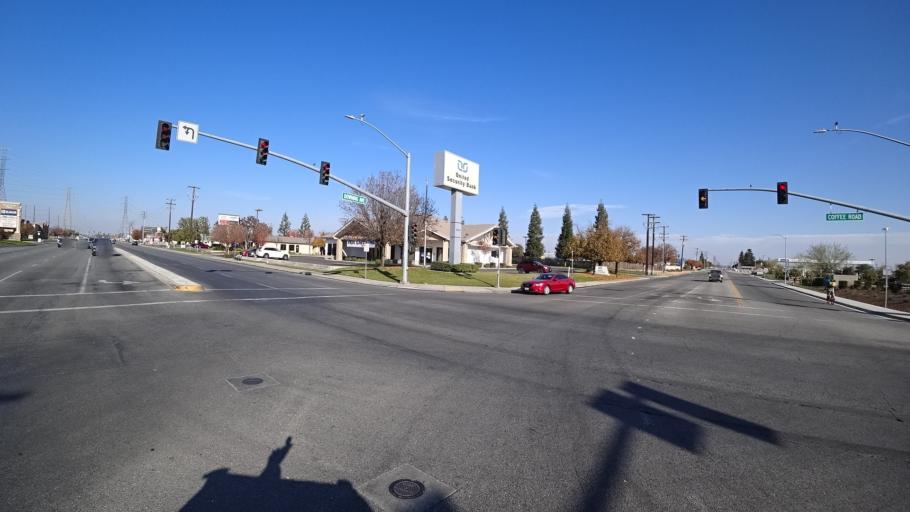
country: US
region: California
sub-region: Kern County
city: Greenacres
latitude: 35.3906
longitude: -119.0922
